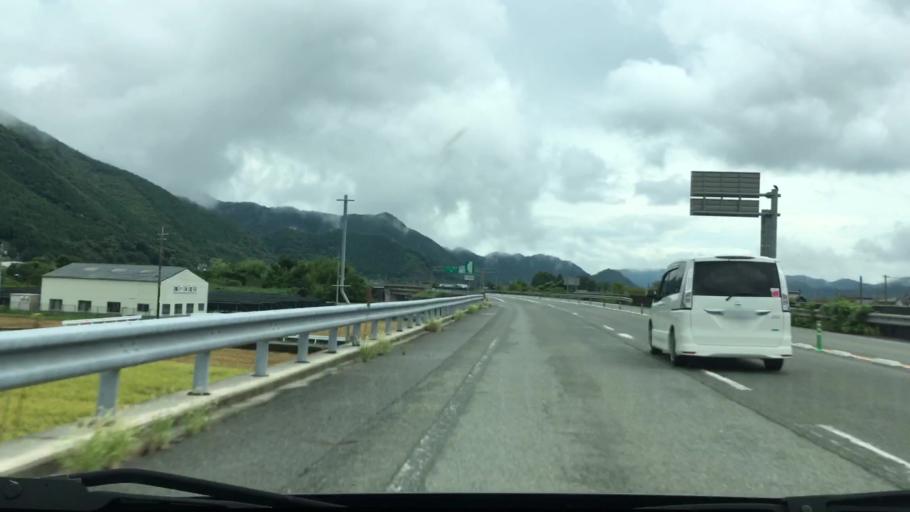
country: JP
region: Hyogo
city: Yamazakicho-nakabirose
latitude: 35.0516
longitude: 134.7639
